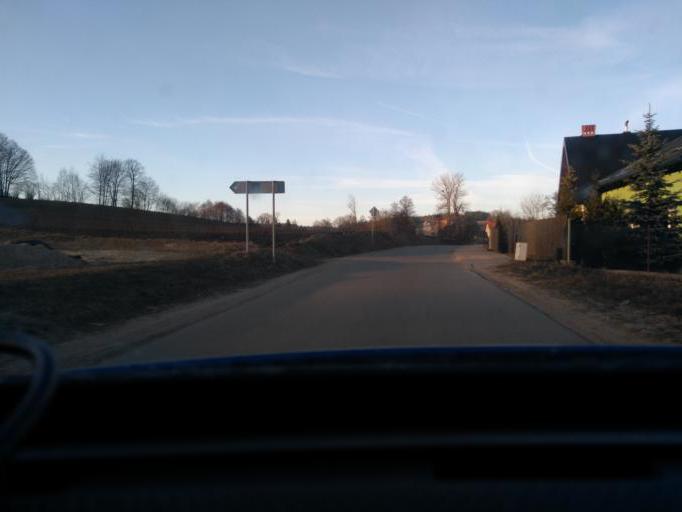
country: PL
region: Pomeranian Voivodeship
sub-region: Powiat kartuski
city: Przodkowo
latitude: 54.3732
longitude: 18.2645
